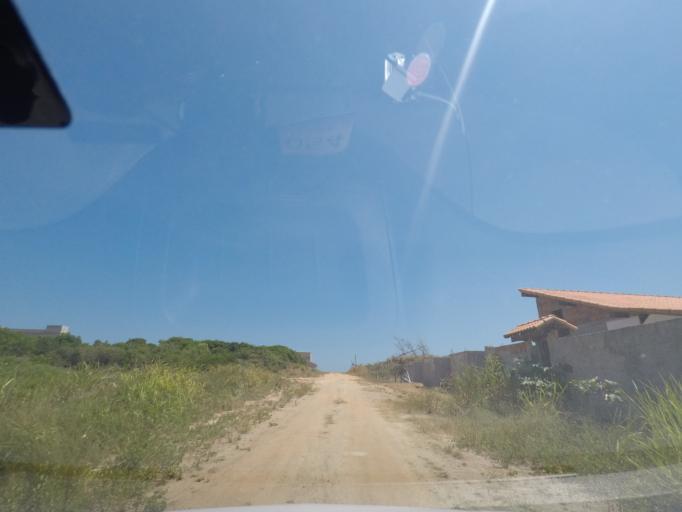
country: BR
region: Rio de Janeiro
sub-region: Marica
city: Marica
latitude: -22.9720
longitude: -42.9307
